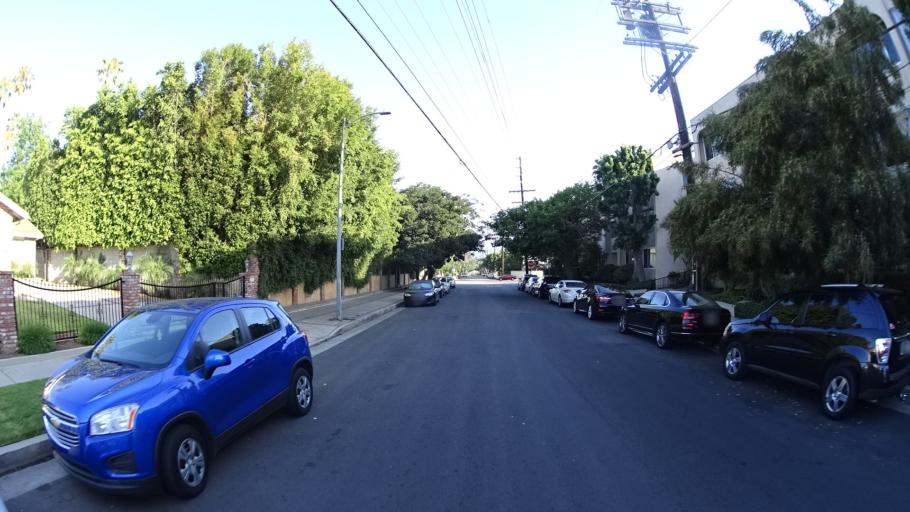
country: US
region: California
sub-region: Los Angeles County
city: Van Nuys
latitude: 34.1693
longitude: -118.4443
